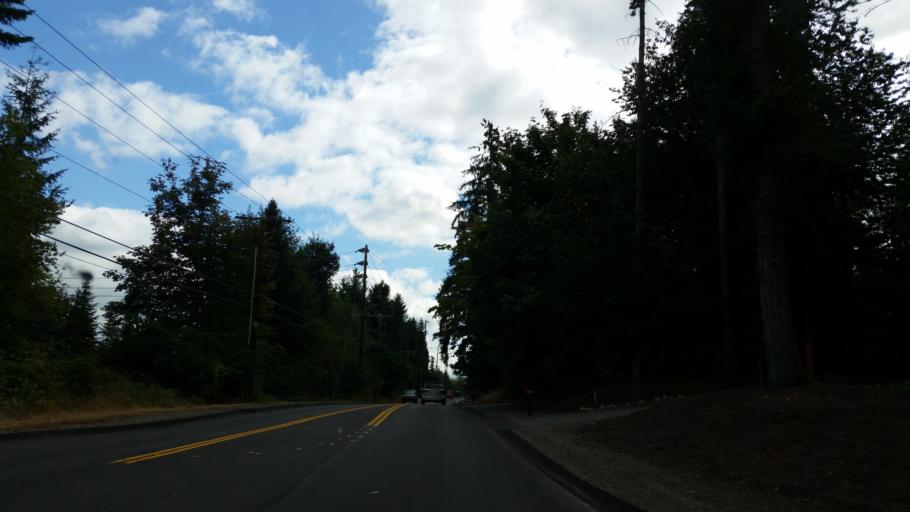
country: US
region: Washington
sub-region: Pierce County
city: Bonney Lake
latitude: 47.2266
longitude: -122.1441
